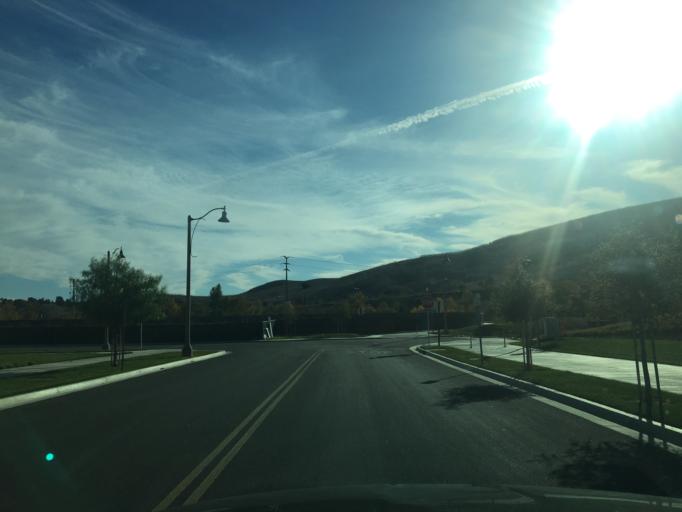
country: US
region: California
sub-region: Orange County
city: Laguna Woods
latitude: 33.6367
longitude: -117.7476
